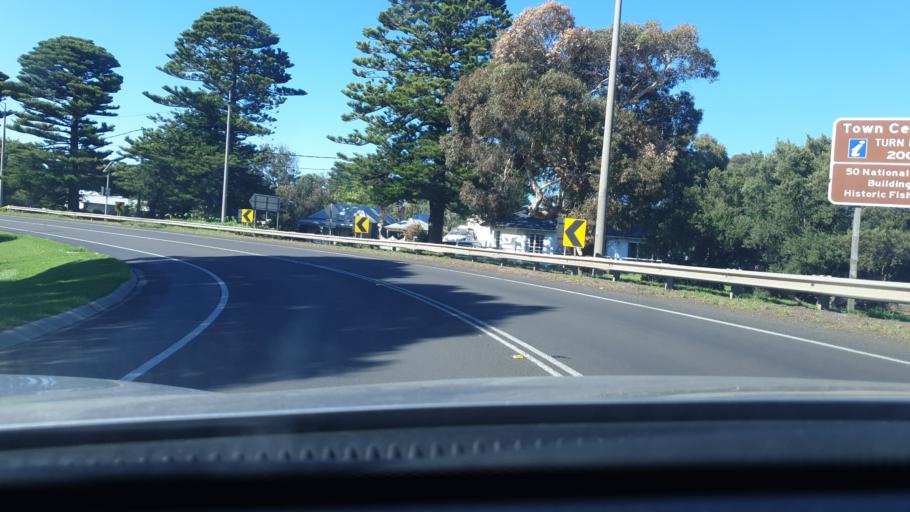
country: AU
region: Victoria
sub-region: Moyne
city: Port Fairy
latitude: -38.3846
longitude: 142.2283
